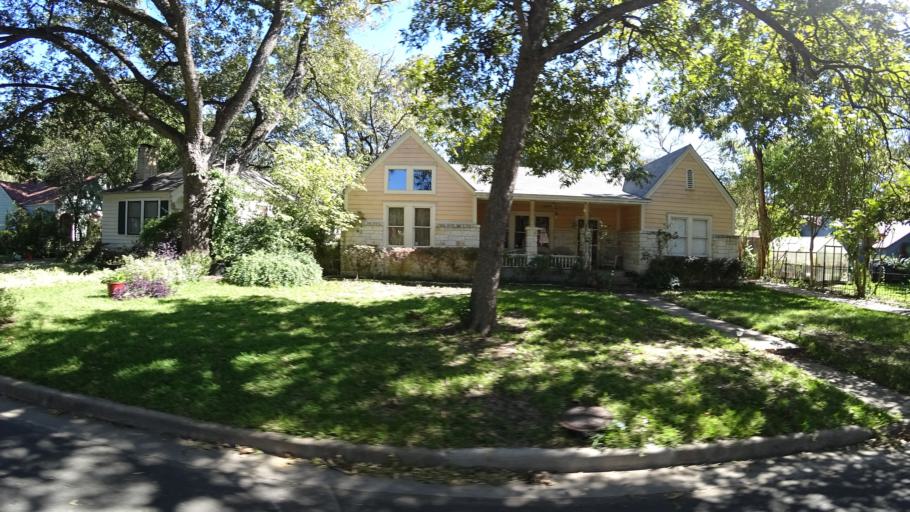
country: US
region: Texas
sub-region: Travis County
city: Austin
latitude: 30.3156
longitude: -97.7449
